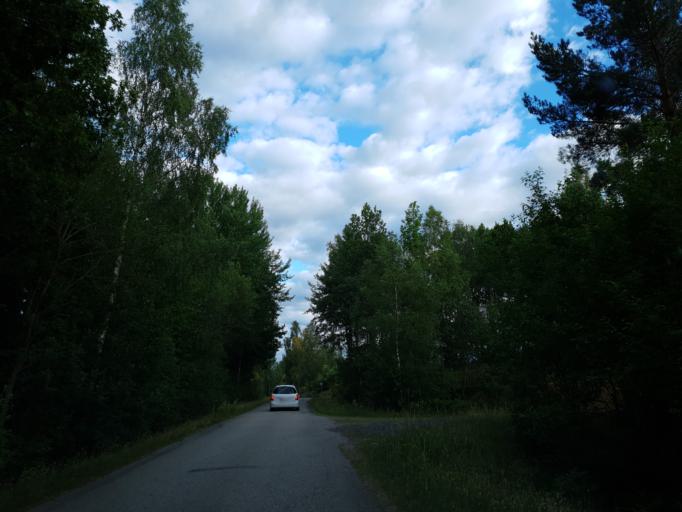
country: SE
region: Kalmar
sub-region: Emmaboda Kommun
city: Emmaboda
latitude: 56.6254
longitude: 15.6448
